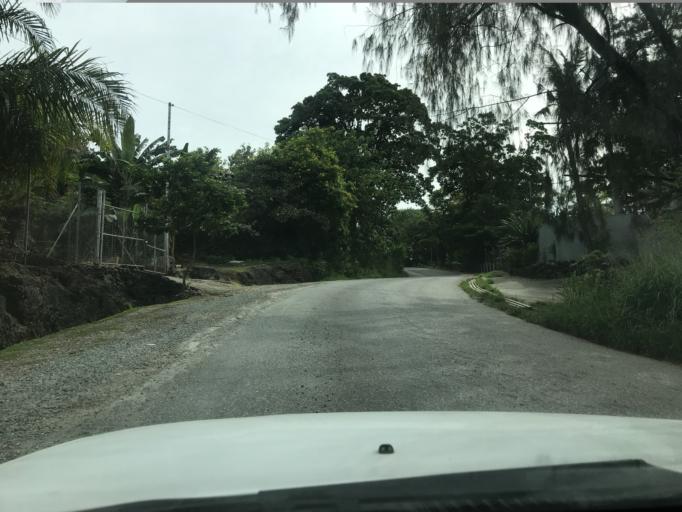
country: SB
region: Guadalcanal
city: Honiara
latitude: -9.4320
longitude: 159.9459
